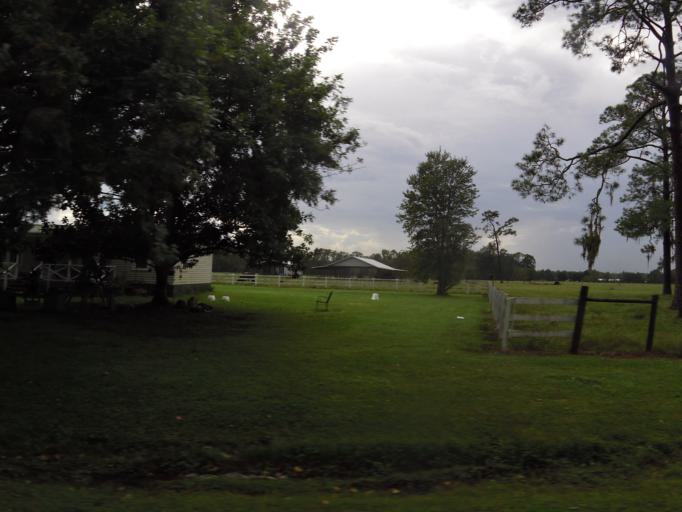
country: US
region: Florida
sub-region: Duval County
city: Baldwin
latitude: 30.3247
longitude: -81.8970
